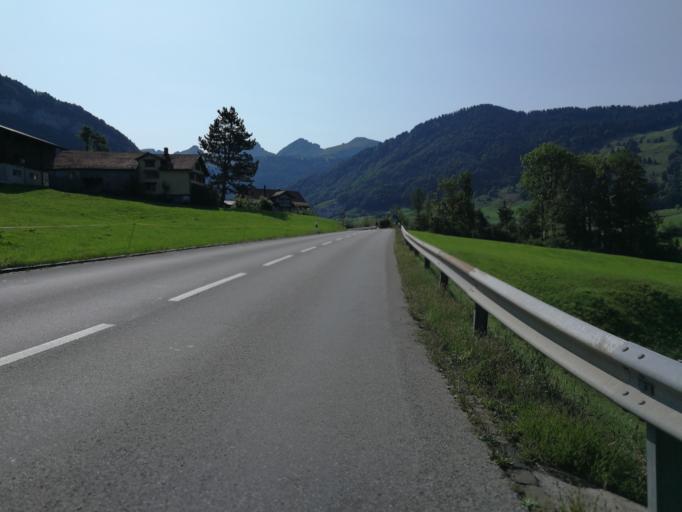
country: CH
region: Saint Gallen
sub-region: Wahlkreis Toggenburg
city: Krummenau
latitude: 47.2060
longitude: 9.2205
